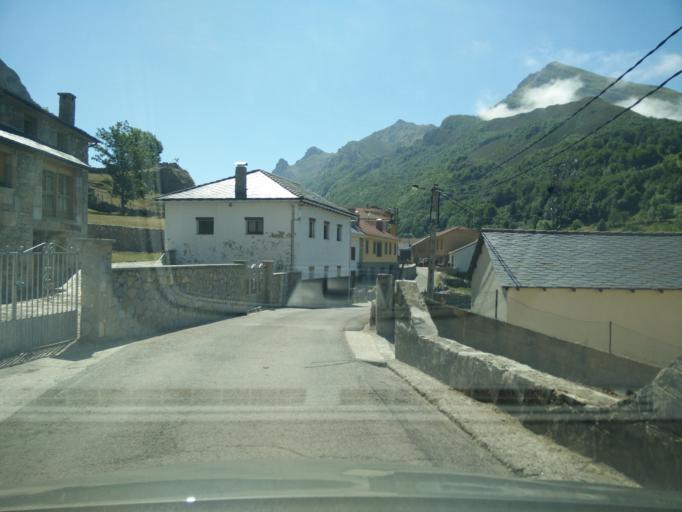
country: ES
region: Asturias
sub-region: Province of Asturias
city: Pola de Somiedo
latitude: 43.0728
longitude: -6.2000
